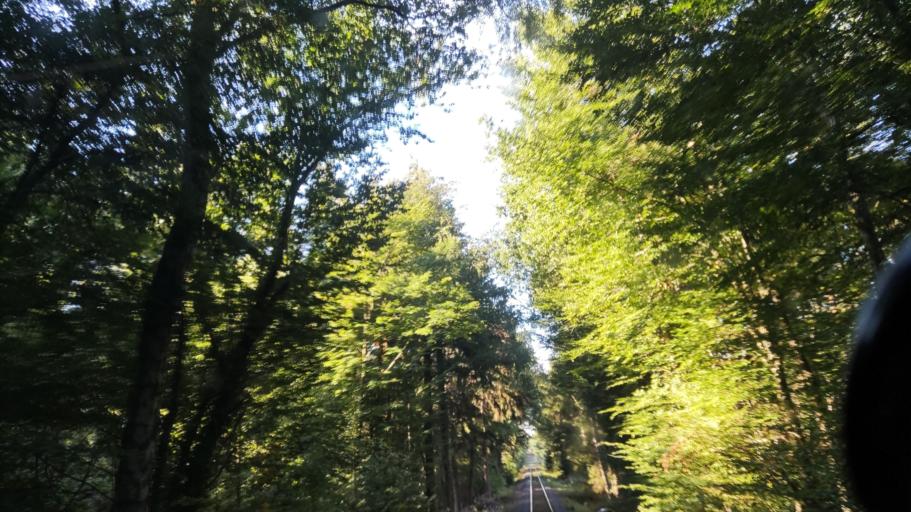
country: DE
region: Lower Saxony
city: Embsen
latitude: 53.1693
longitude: 10.3624
